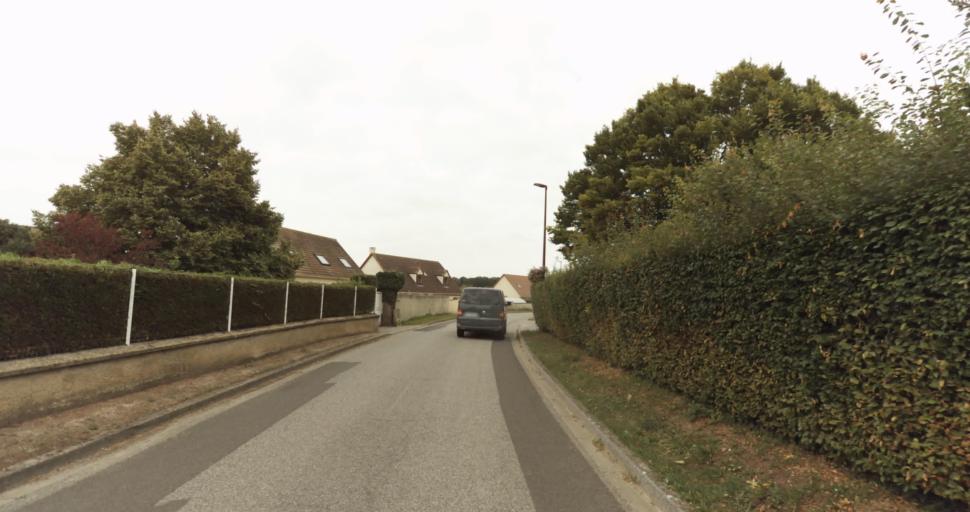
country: FR
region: Haute-Normandie
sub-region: Departement de l'Eure
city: Marcilly-sur-Eure
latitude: 48.8240
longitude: 1.3156
